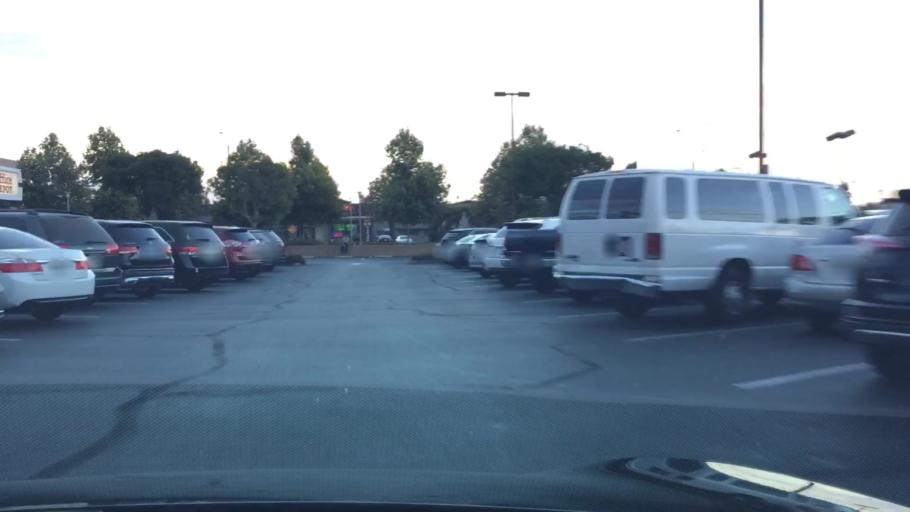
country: US
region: California
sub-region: Los Angeles County
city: Temple City
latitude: 34.0998
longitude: -118.0744
